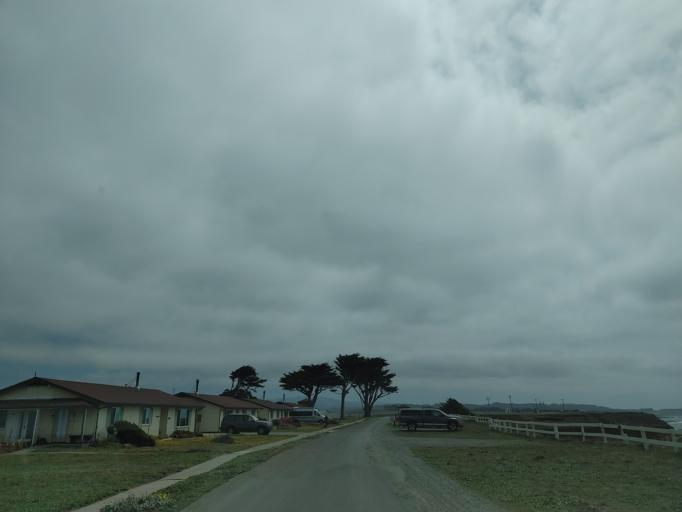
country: US
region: California
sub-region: Sonoma County
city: Sea Ranch
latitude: 38.9540
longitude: -123.7396
